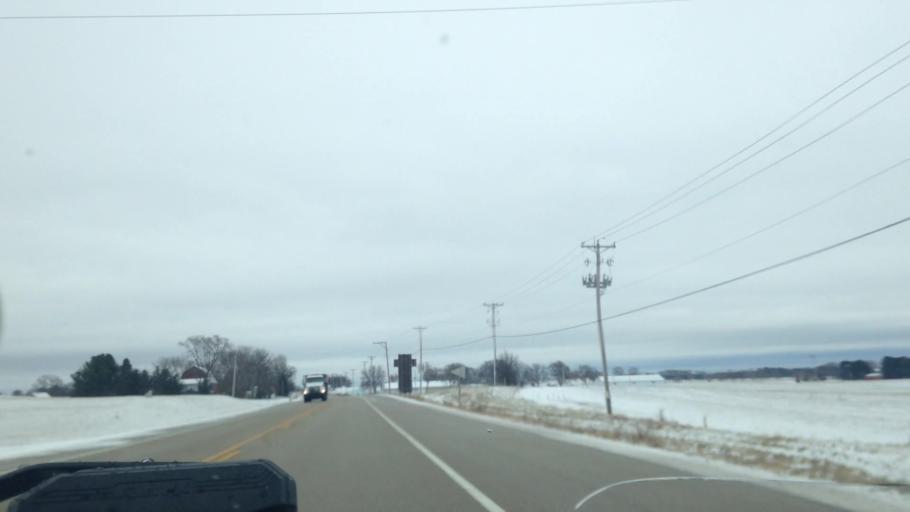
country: US
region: Wisconsin
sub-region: Dodge County
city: Beaver Dam
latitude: 43.4442
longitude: -88.7673
